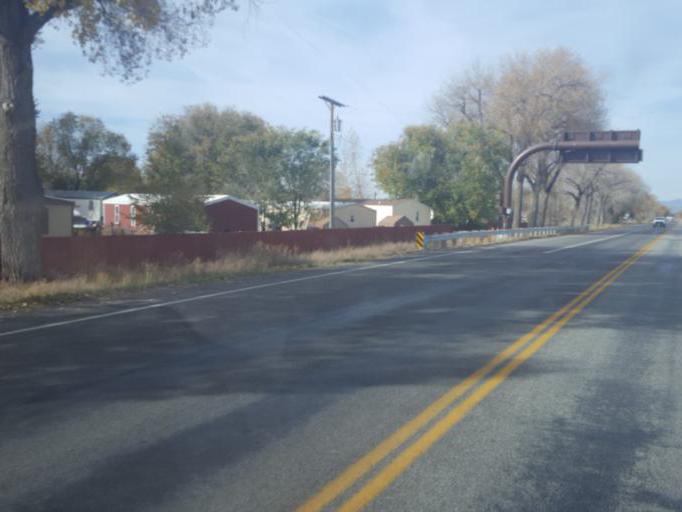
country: US
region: Colorado
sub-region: Alamosa County
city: Alamosa East
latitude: 37.4735
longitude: -105.8347
